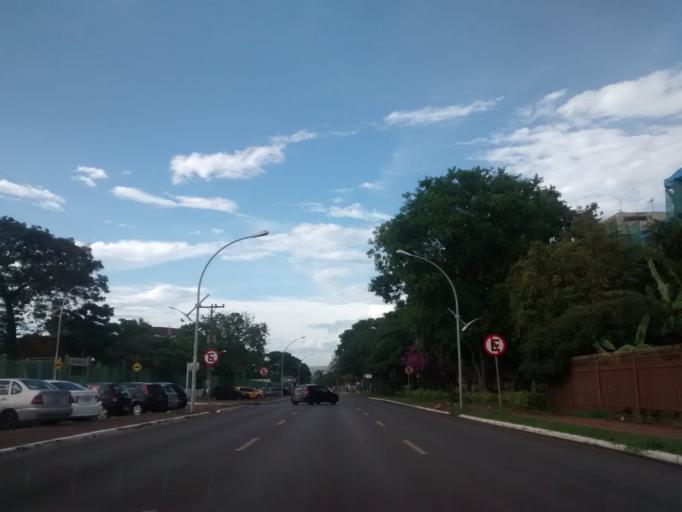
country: BR
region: Federal District
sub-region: Brasilia
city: Brasilia
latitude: -15.7690
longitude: -47.8924
